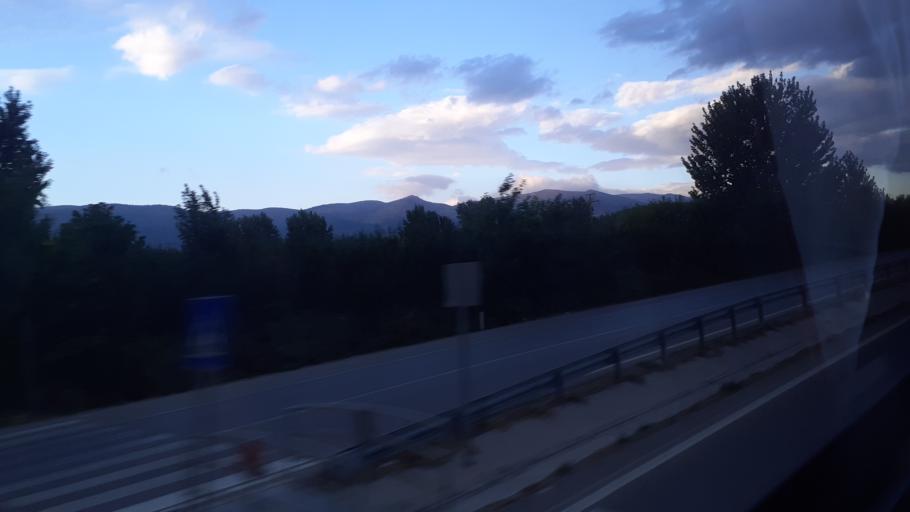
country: TR
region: Tokat
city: Dokmetepe
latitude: 40.3211
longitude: 36.1955
